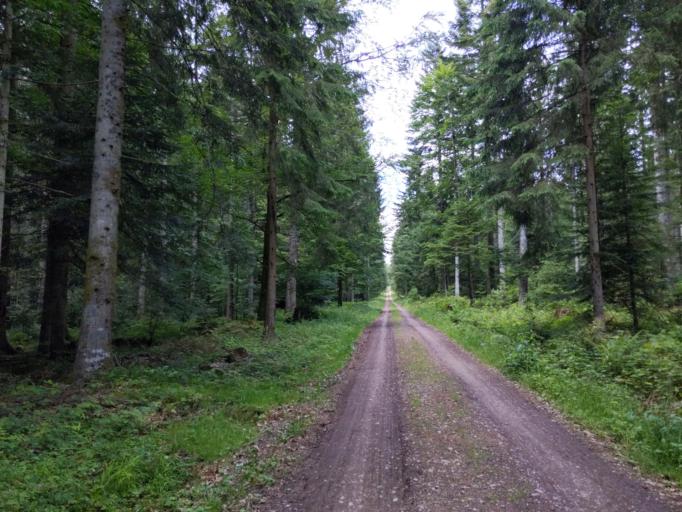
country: DE
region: Baden-Wuerttemberg
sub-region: Karlsruhe Region
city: Freudenstadt
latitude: 48.4250
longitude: 8.3989
